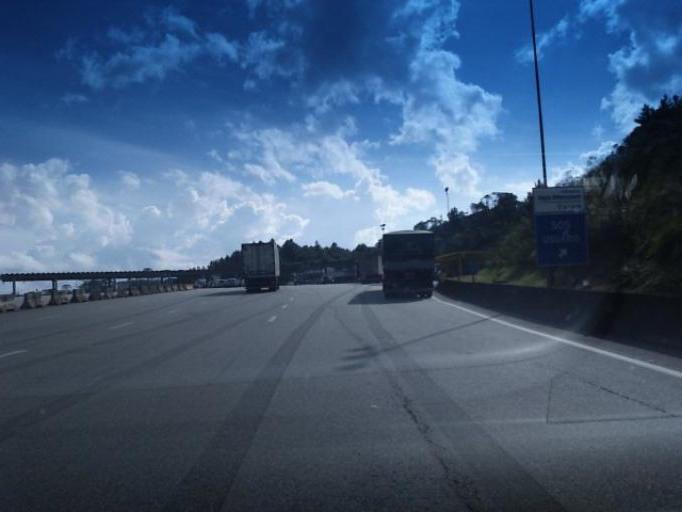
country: BR
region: Parana
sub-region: Campina Grande Do Sul
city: Campina Grande do Sul
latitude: -25.2879
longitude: -48.9328
